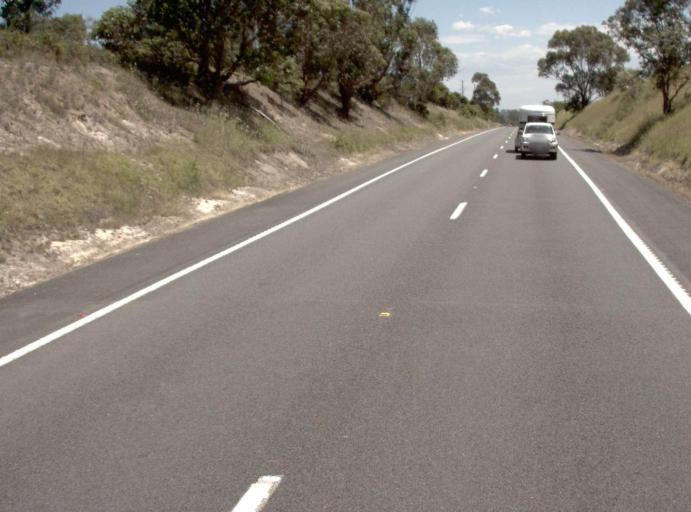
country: AU
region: Victoria
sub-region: East Gippsland
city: Lakes Entrance
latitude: -37.7037
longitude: 148.4749
